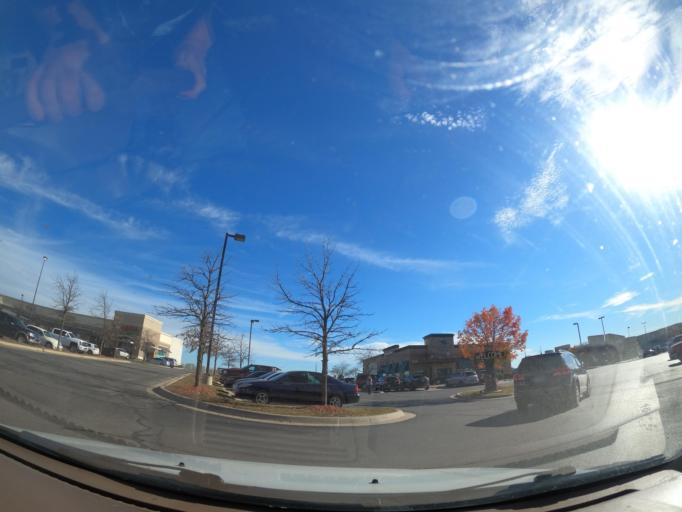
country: US
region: Oklahoma
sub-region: Tulsa County
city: Owasso
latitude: 36.2897
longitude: -95.8415
